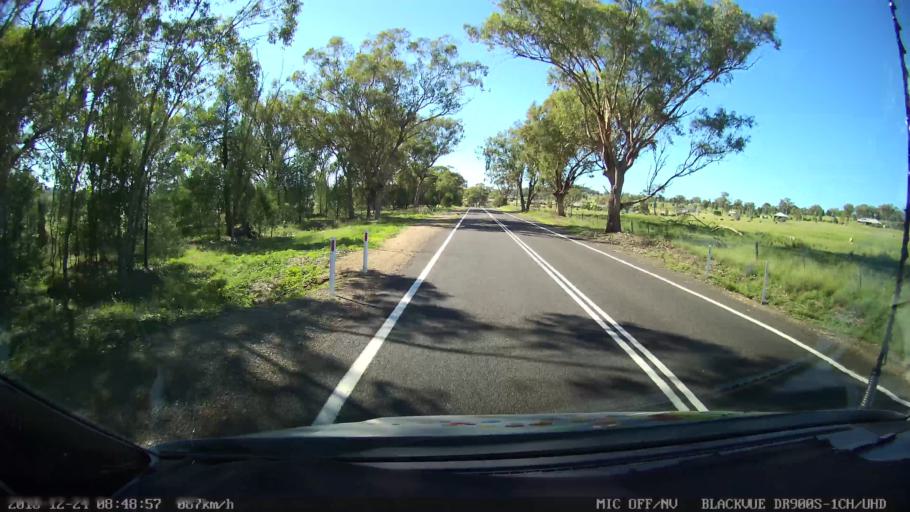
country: AU
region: New South Wales
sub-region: Liverpool Plains
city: Quirindi
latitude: -31.4618
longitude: 150.6495
